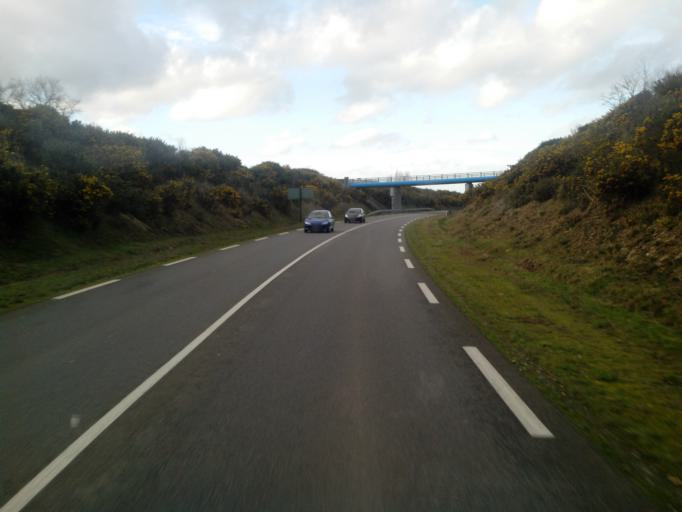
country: FR
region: Brittany
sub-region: Departement d'Ille-et-Vilaine
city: Pleurtuit
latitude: 48.5691
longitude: -2.0668
